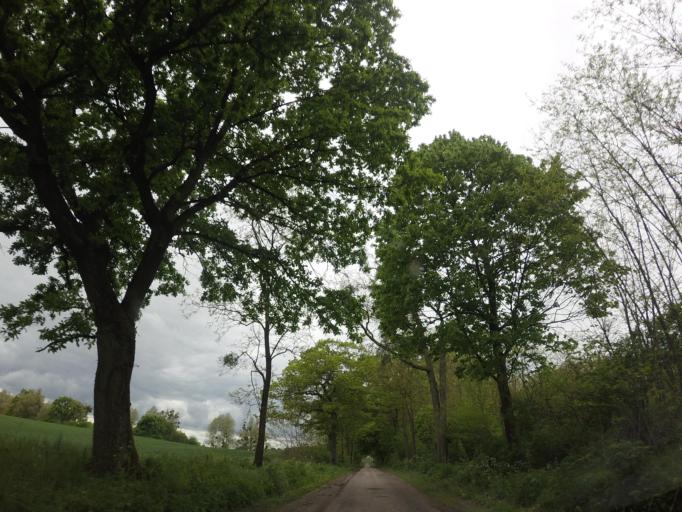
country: PL
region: West Pomeranian Voivodeship
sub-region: Powiat choszczenski
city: Choszczno
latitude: 53.1743
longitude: 15.3152
